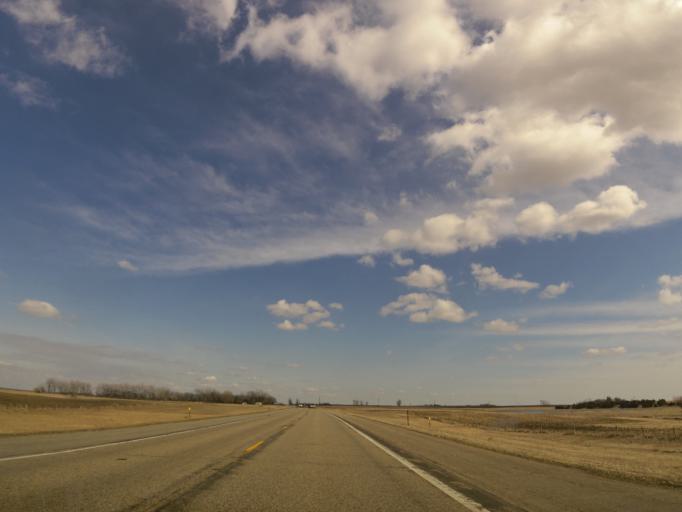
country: US
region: South Dakota
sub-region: Deuel County
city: Clear Lake
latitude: 44.9334
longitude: -96.6518
